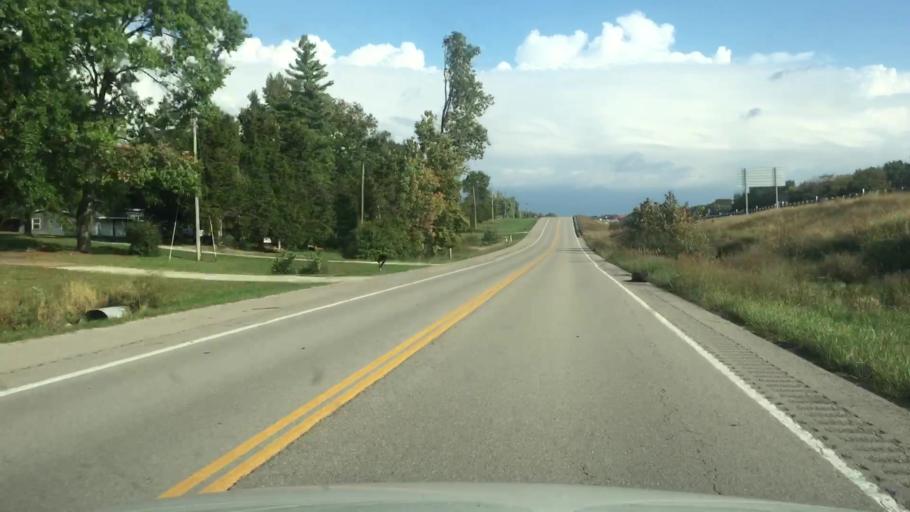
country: US
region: Missouri
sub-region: Boone County
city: Ashland
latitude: 38.8467
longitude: -92.2497
